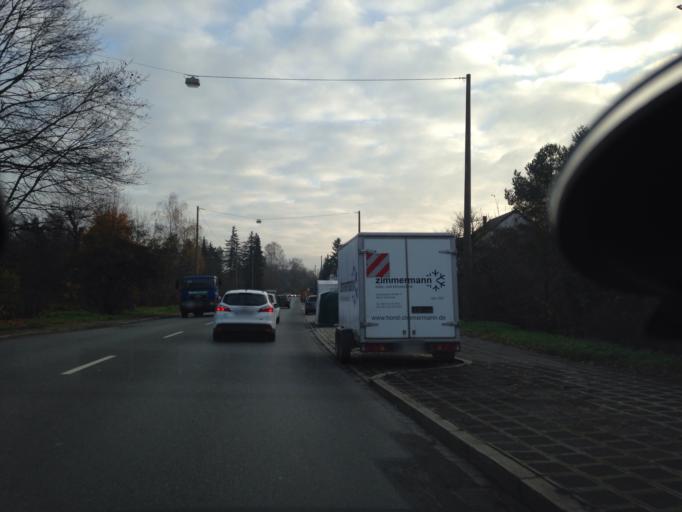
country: DE
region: Bavaria
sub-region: Regierungsbezirk Mittelfranken
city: Schwaig
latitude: 49.4682
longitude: 11.1596
